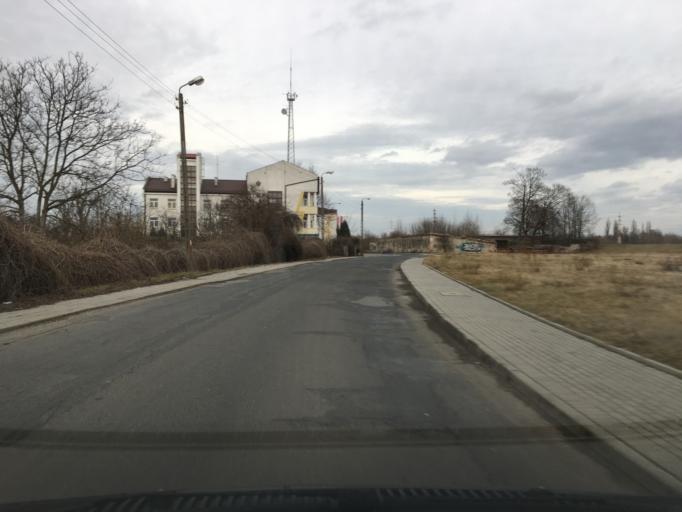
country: PL
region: Opole Voivodeship
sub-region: Powiat kedzierzynsko-kozielski
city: Kozle
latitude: 50.3418
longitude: 18.1436
